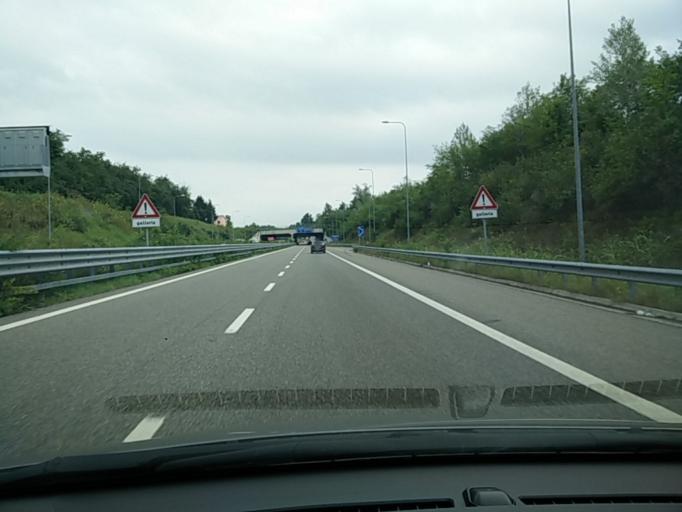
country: IT
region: Lombardy
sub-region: Provincia di Varese
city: Lonate Pozzolo
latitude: 45.5753
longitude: 8.7361
